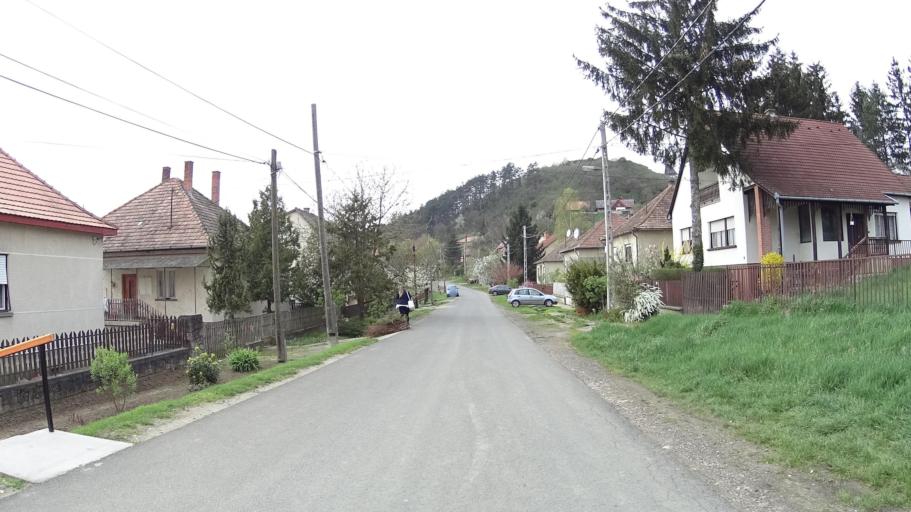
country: HU
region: Nograd
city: Diosjeno
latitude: 47.9045
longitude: 19.0493
